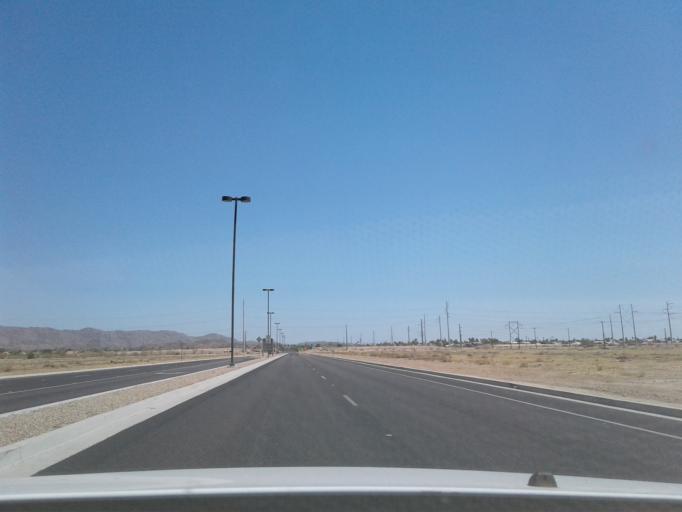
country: US
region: Arizona
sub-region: Maricopa County
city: Guadalupe
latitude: 33.2856
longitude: -111.9971
